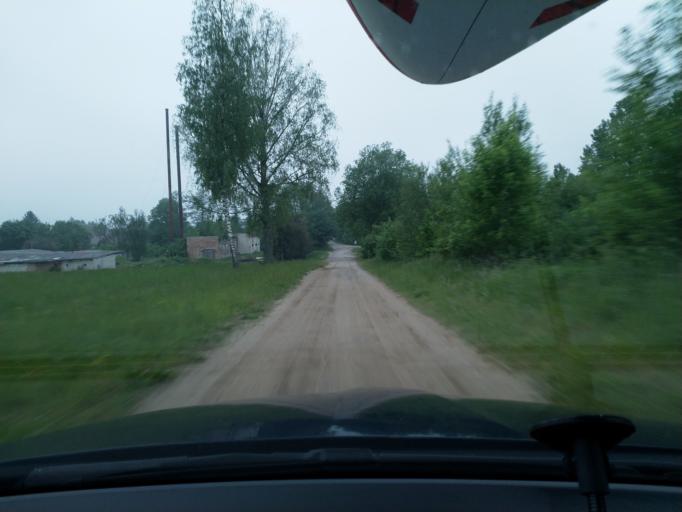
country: LV
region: Kuldigas Rajons
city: Kuldiga
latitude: 56.8793
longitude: 21.8242
